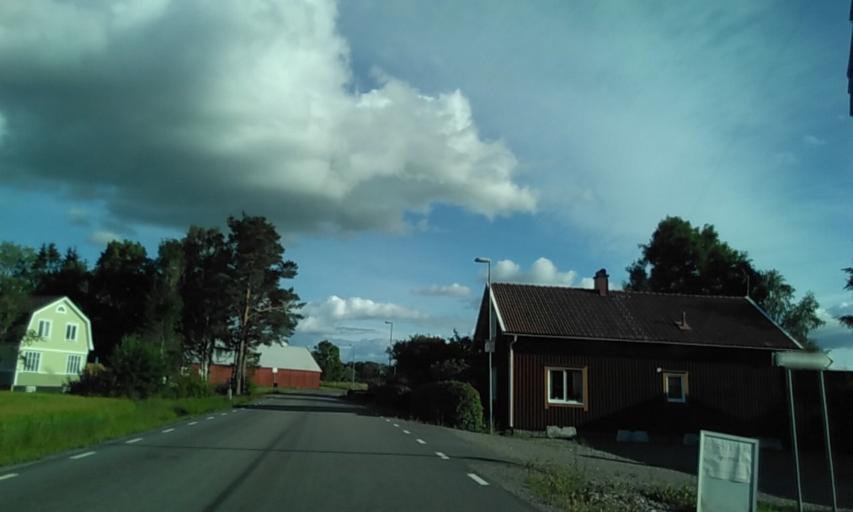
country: SE
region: Vaestra Goetaland
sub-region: Vara Kommun
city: Vara
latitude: 58.4078
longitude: 12.9157
